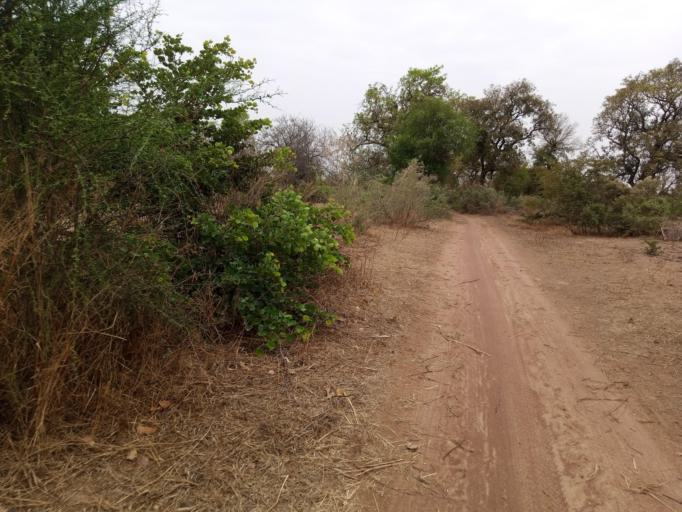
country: BF
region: Boucle du Mouhoun
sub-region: Province de la Kossi
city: Nouna
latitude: 12.8426
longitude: -4.0770
